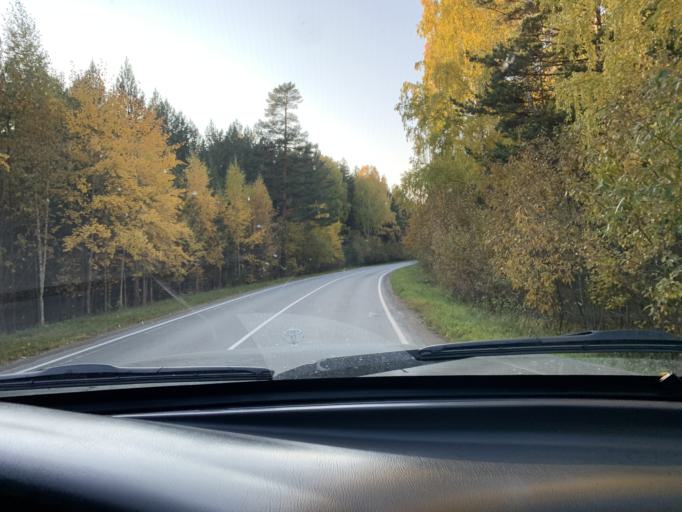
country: RU
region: Sverdlovsk
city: Verkhneye Dubrovo
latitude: 56.8650
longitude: 61.0875
